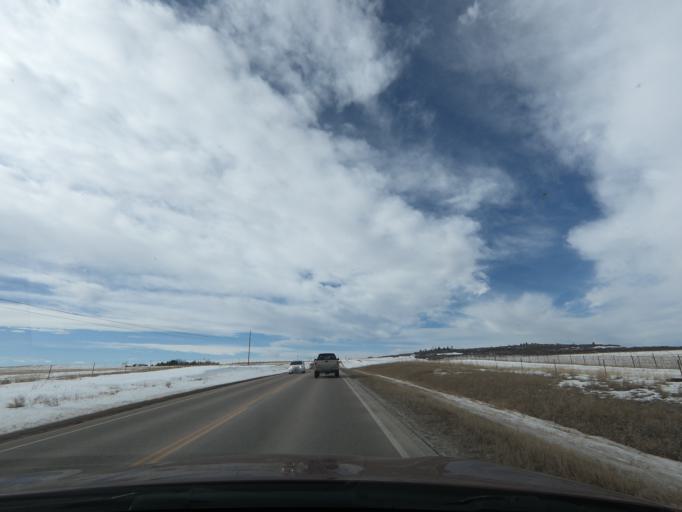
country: US
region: Colorado
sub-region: Elbert County
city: Elizabeth
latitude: 39.2651
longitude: -104.7211
